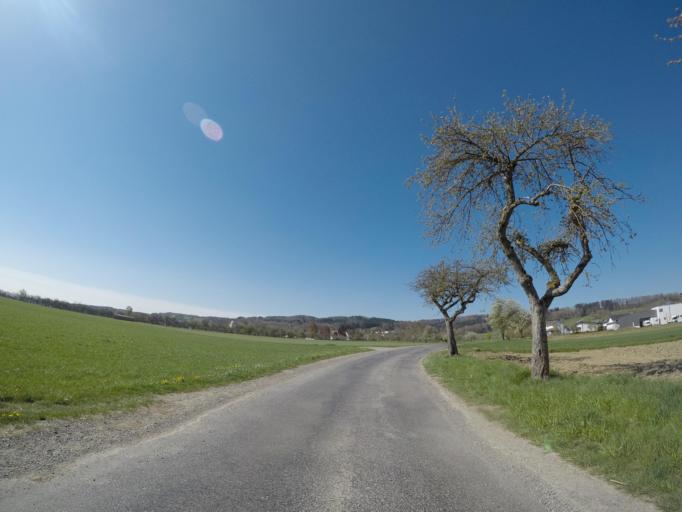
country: DE
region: Baden-Wuerttemberg
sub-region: Tuebingen Region
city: Wilhelmsdorf
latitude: 47.8542
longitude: 9.4342
